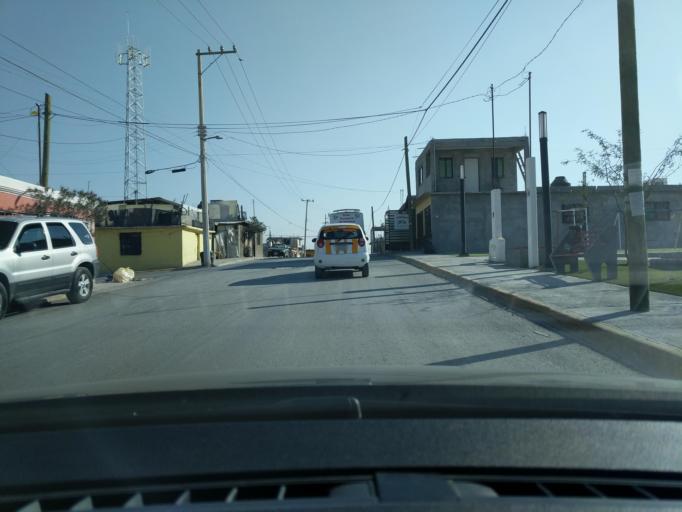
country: MX
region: Coahuila
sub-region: Ramos Arizpe
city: Ramos Arizpe
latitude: 25.5583
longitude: -100.9604
